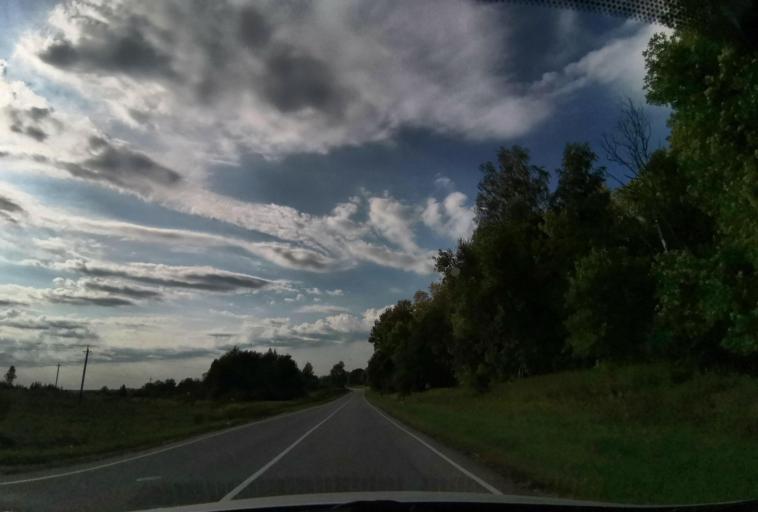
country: RU
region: Kaliningrad
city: Neman
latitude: 55.0174
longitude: 22.1093
